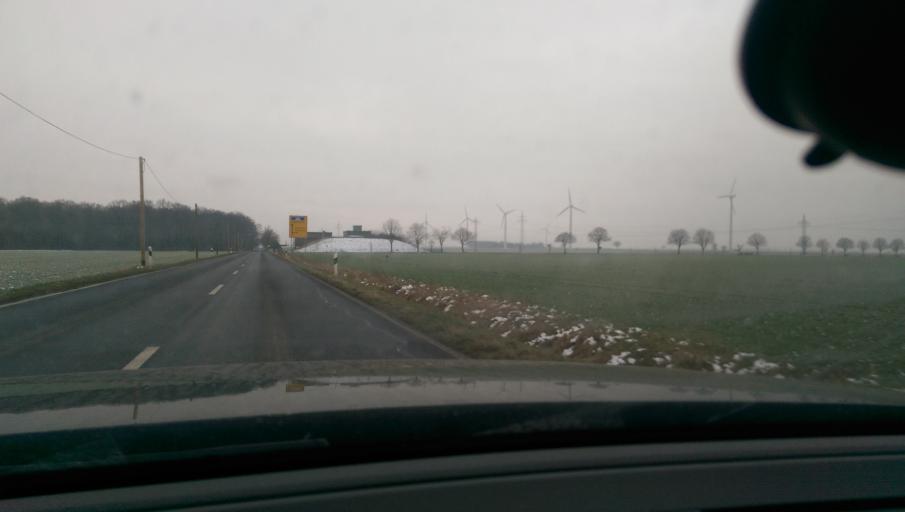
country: DE
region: Lower Saxony
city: Gross Munzel
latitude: 52.3913
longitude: 9.5133
